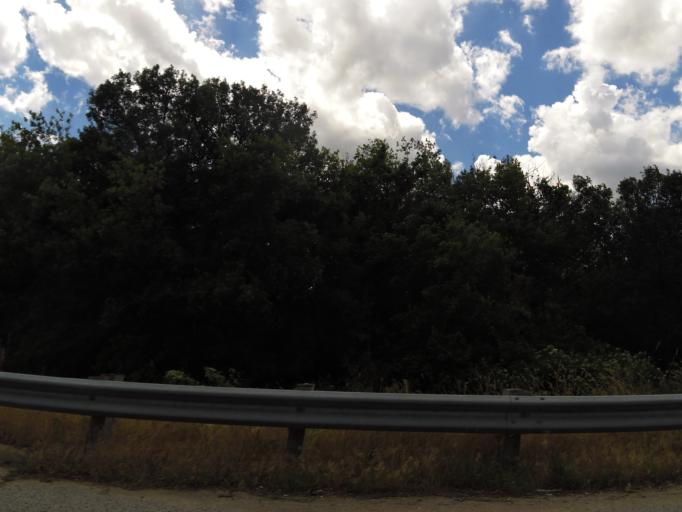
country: US
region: Iowa
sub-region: Fayette County
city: Oelwein
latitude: 42.6225
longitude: -91.9070
